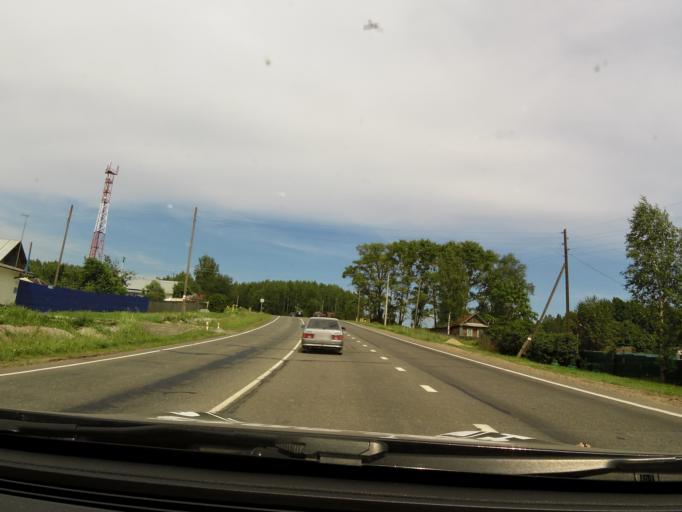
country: RU
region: Kirov
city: Vakhrushi
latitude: 58.6598
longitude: 49.9215
